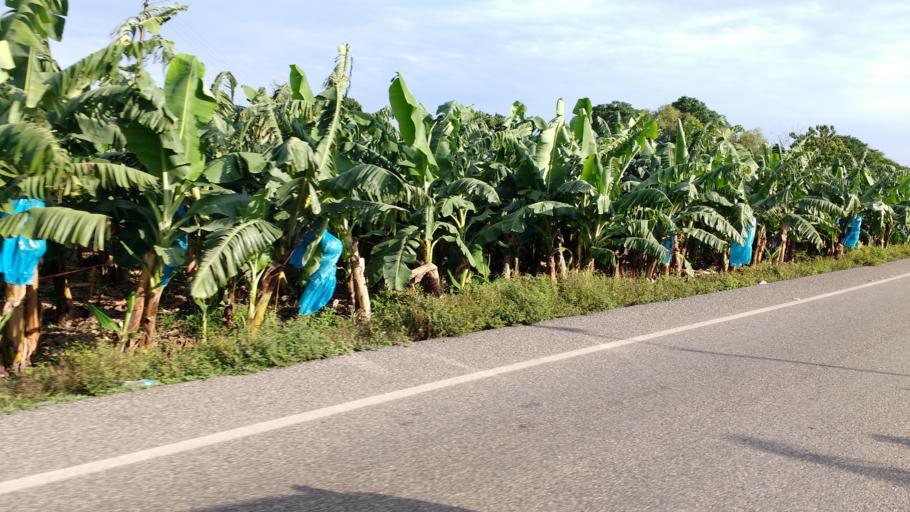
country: MX
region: Tabasco
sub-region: Teapa
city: Eureka y Belen
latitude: 17.6225
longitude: -92.9625
